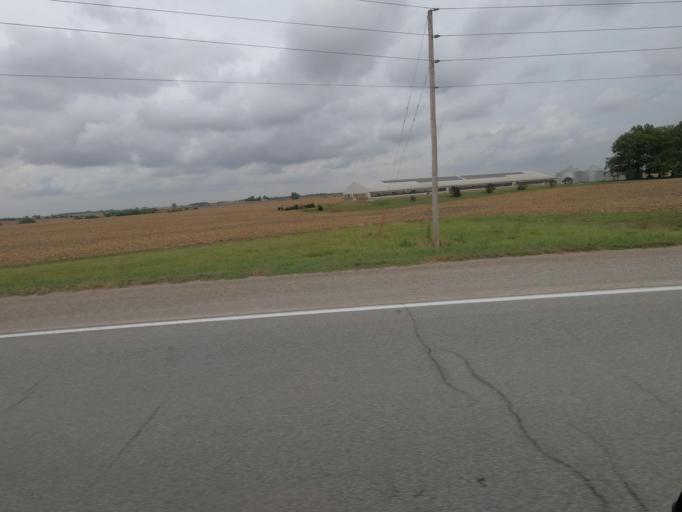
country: US
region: Iowa
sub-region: Wapello County
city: Ottumwa
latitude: 40.9499
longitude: -92.2294
